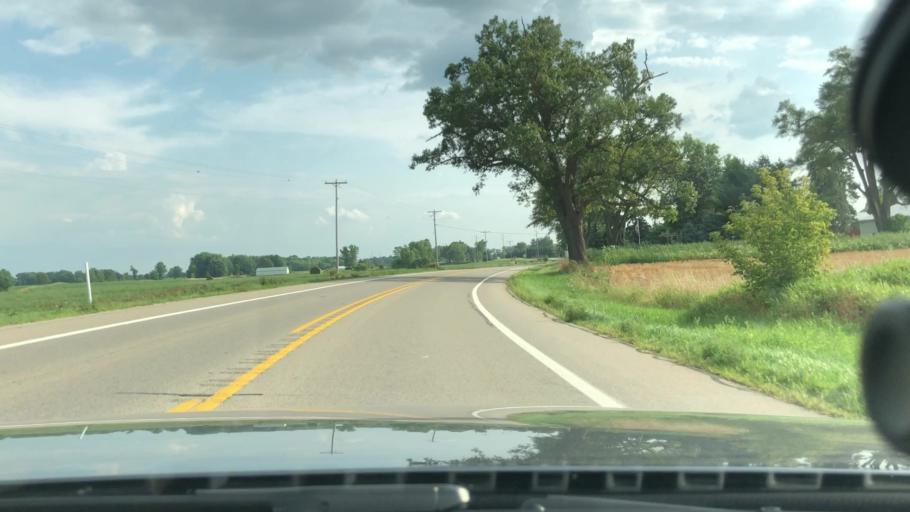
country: US
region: Michigan
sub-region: Washtenaw County
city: Chelsea
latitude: 42.2767
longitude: -84.0317
